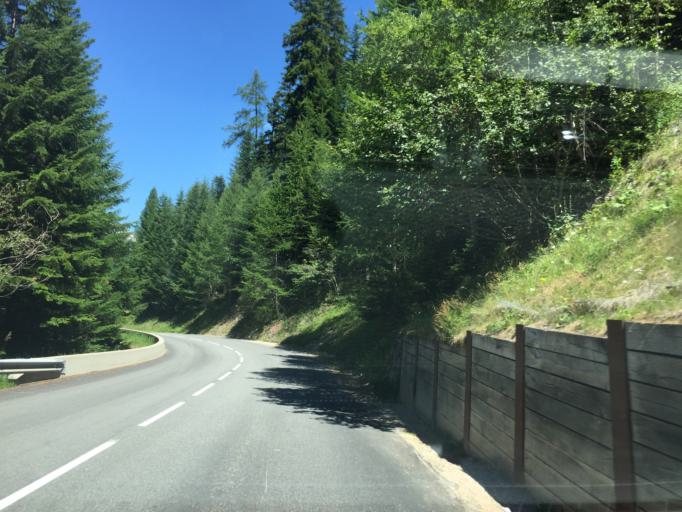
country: FR
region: Rhone-Alpes
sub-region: Departement de la Savoie
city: Modane
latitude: 45.1847
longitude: 6.6596
